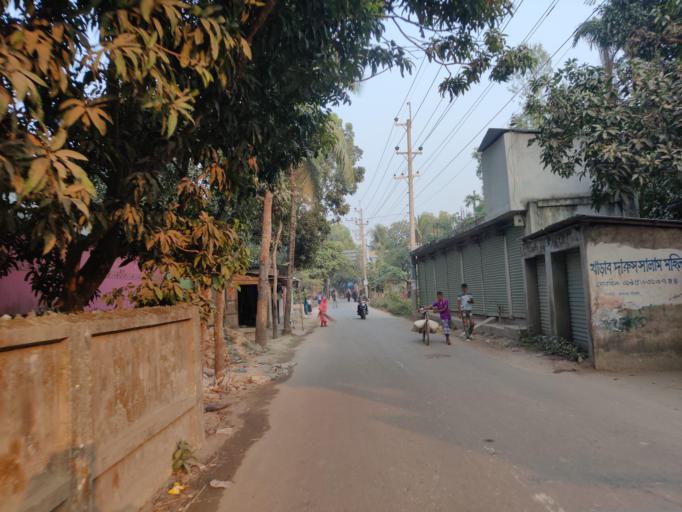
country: BD
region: Dhaka
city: Bajitpur
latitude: 24.1585
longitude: 90.7529
